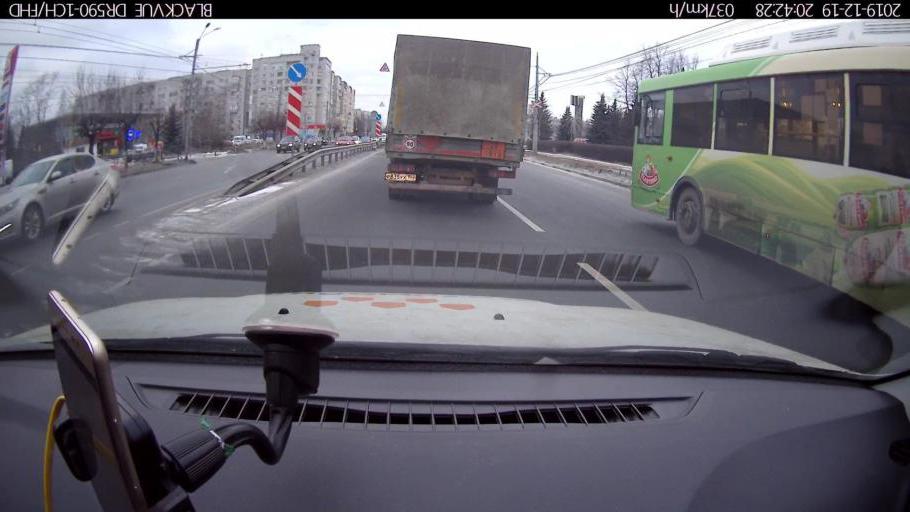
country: RU
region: Nizjnij Novgorod
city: Nizhniy Novgorod
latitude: 56.3228
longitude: 43.8831
